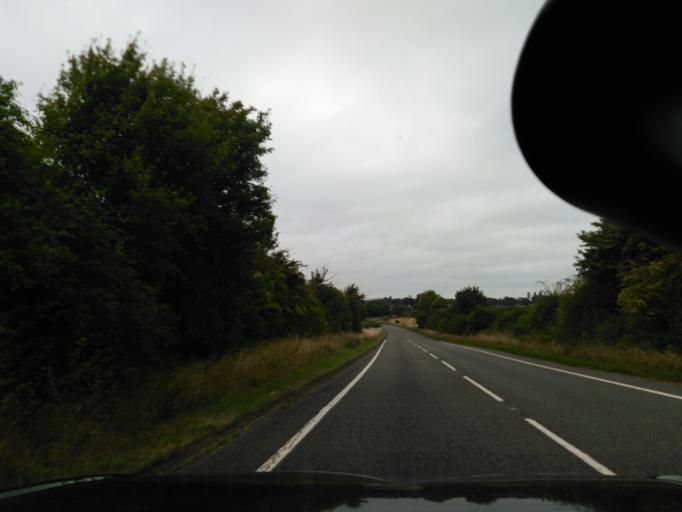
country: GB
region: England
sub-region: Wiltshire
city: Upton Scudamore
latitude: 51.2393
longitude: -2.1880
